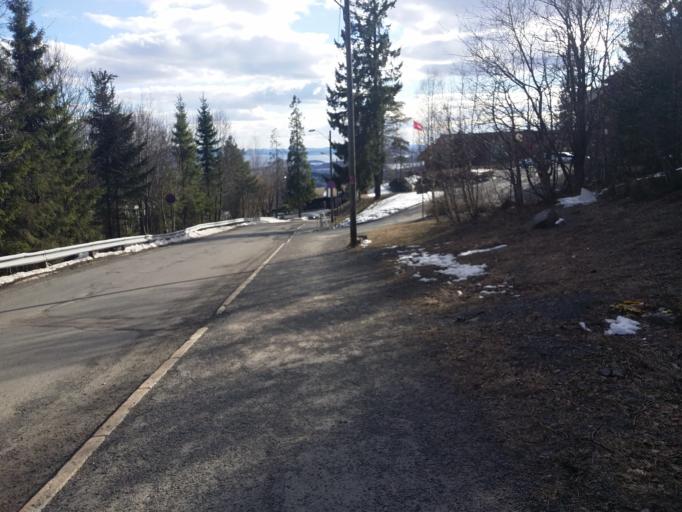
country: NO
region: Oslo
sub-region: Oslo
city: Sjolyststranda
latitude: 59.9634
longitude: 10.6656
